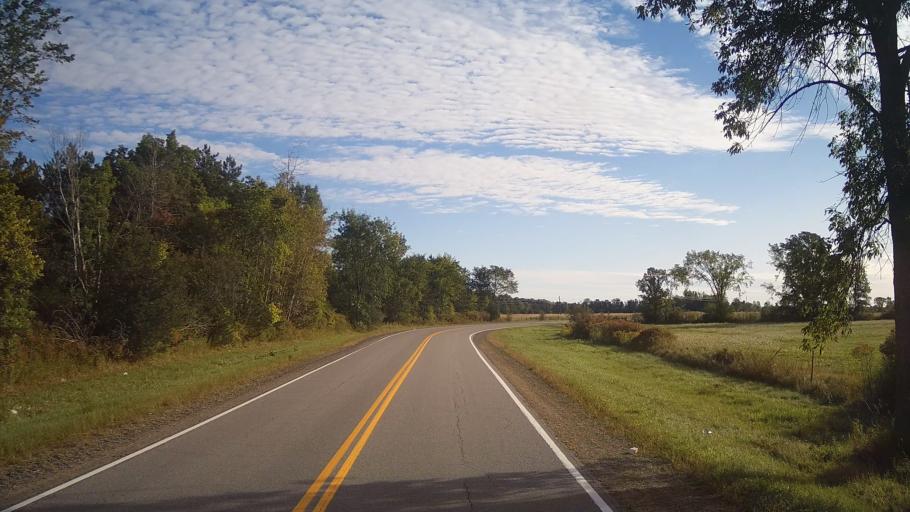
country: CA
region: Ontario
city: Gananoque
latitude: 44.3897
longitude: -76.1247
